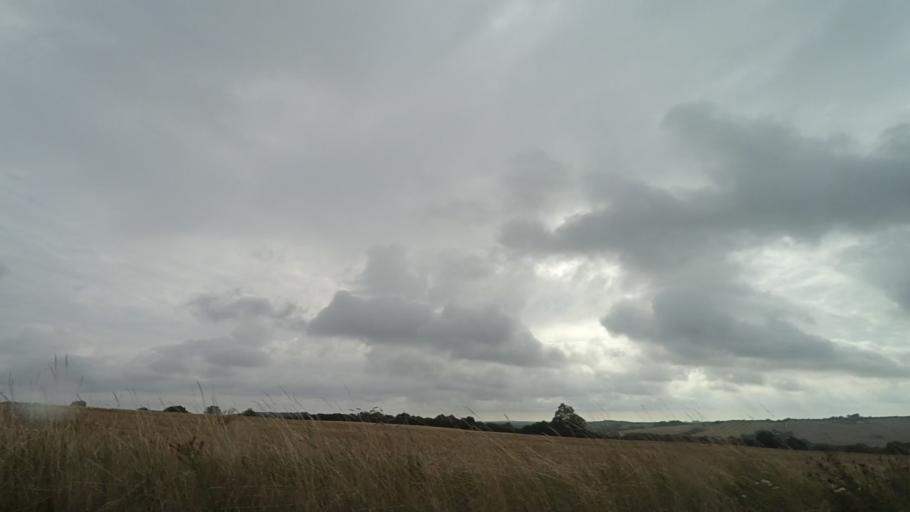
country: DK
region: Central Jutland
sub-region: Syddjurs Kommune
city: Ronde
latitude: 56.3201
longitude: 10.4596
